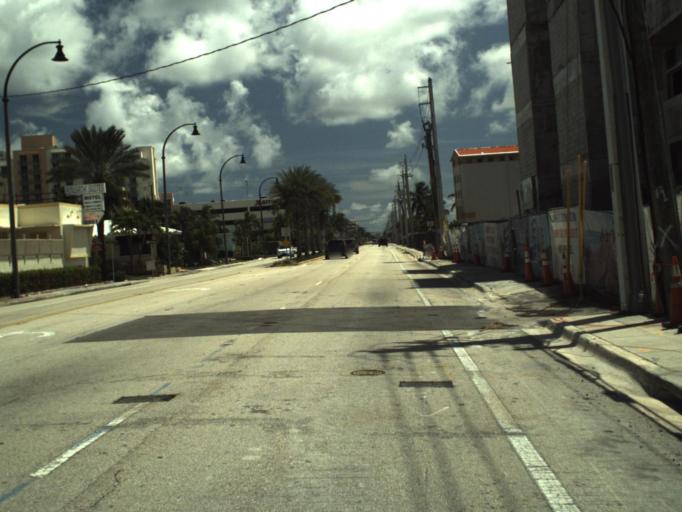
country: US
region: Florida
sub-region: Broward County
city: Dania Beach
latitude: 26.0298
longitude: -80.1159
